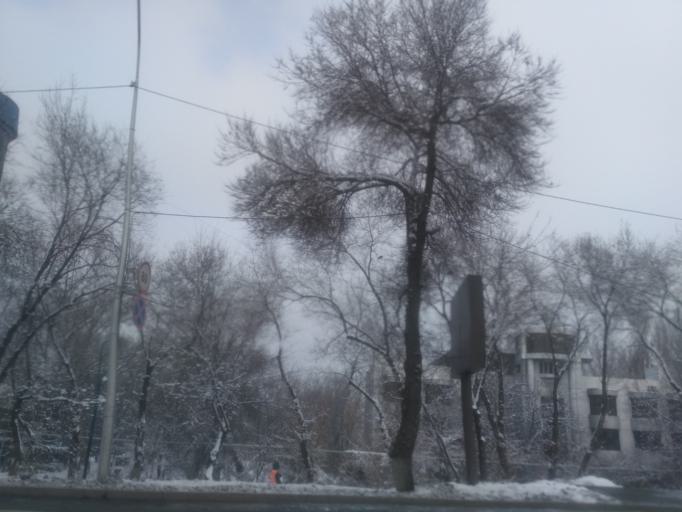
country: KZ
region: Almaty Qalasy
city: Almaty
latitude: 43.2248
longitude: 76.9388
